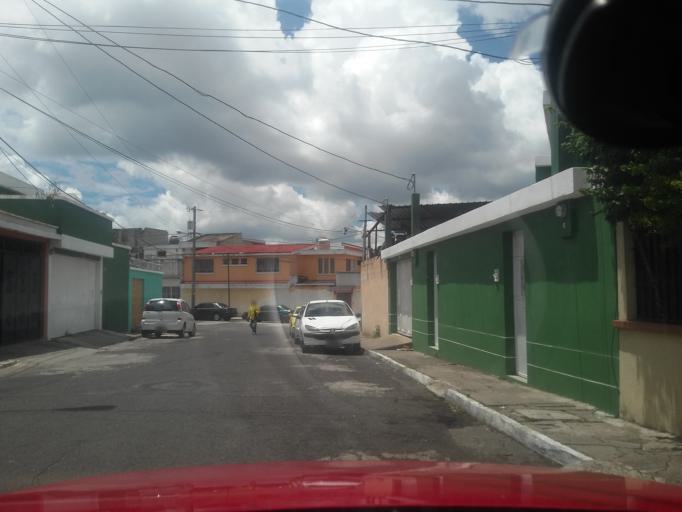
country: GT
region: Guatemala
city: Mixco
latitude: 14.6439
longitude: -90.5669
